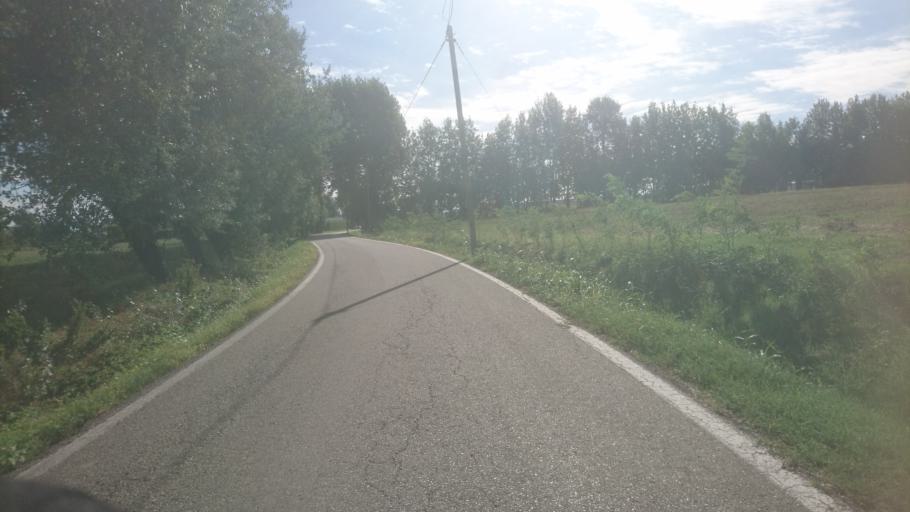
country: IT
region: Veneto
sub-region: Provincia di Vicenza
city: Montegalda
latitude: 45.4624
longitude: 11.6892
